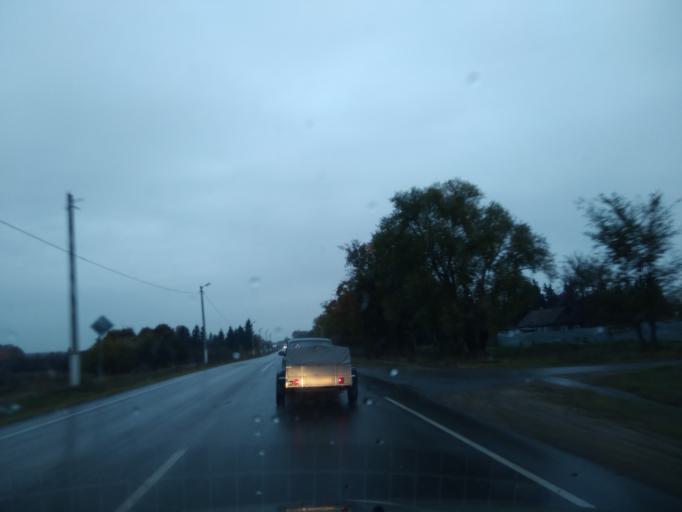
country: RU
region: Tula
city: Kazachka
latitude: 53.3049
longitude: 37.9229
